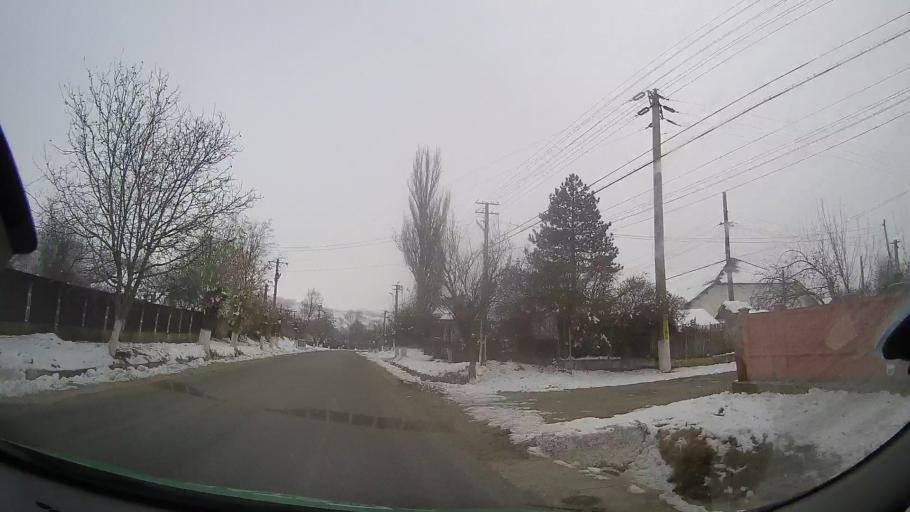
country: RO
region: Bacau
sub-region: Comuna Glavanesti
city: Frumuselu
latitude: 46.2978
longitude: 27.2993
